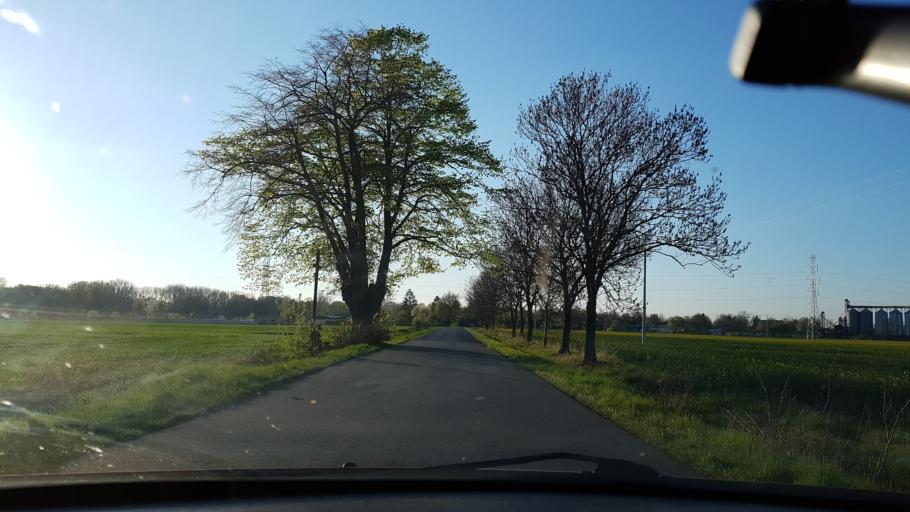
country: PL
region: Opole Voivodeship
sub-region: Powiat nyski
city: Nysa
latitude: 50.4259
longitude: 17.3105
